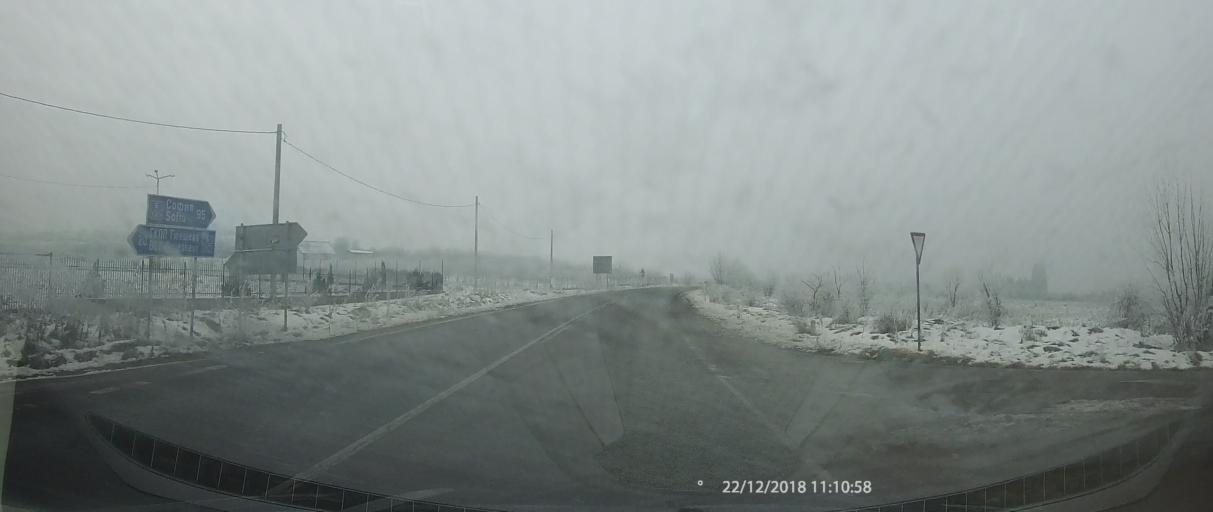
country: BG
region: Kyustendil
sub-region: Obshtina Kyustendil
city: Kyustendil
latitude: 42.2803
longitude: 22.6572
